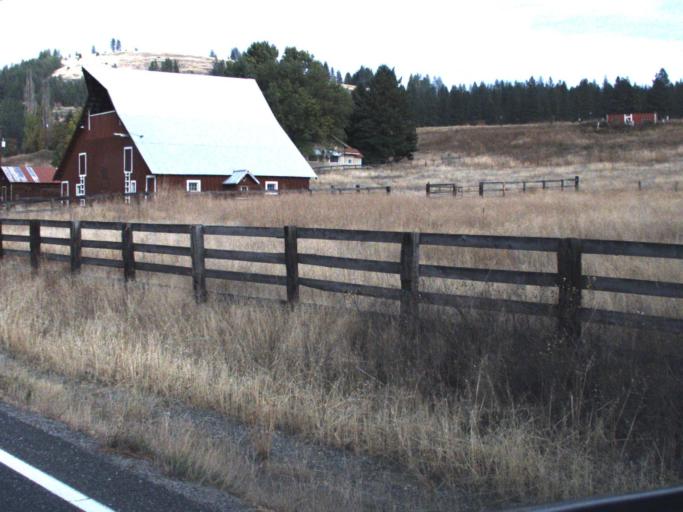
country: US
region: Washington
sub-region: Stevens County
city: Kettle Falls
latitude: 48.7500
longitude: -118.0460
